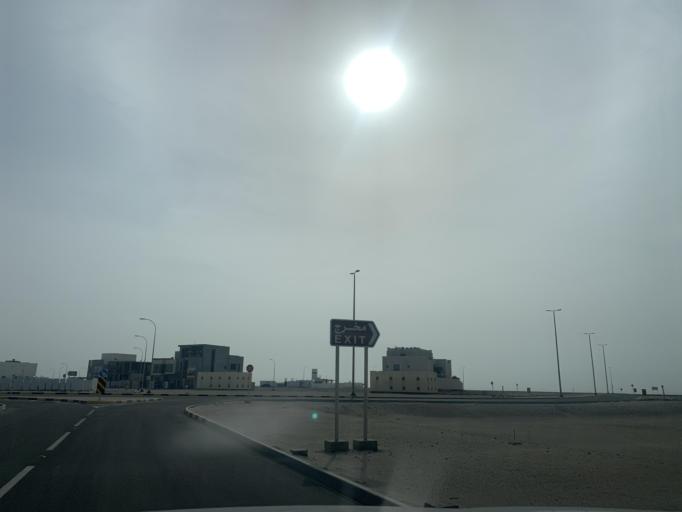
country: BH
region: Muharraq
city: Al Muharraq
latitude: 26.3204
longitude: 50.6250
